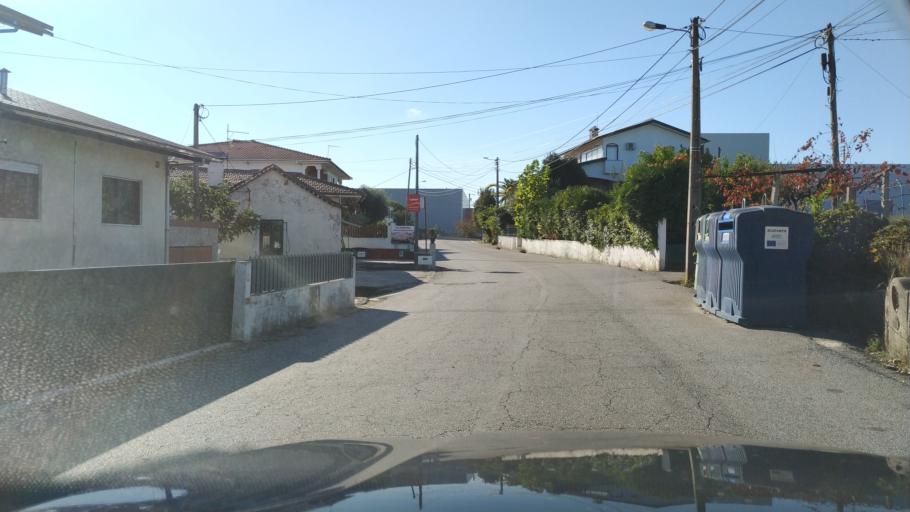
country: PT
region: Aveiro
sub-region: Vale de Cambra
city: Vale de Cambra
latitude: 40.8707
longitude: -8.4145
